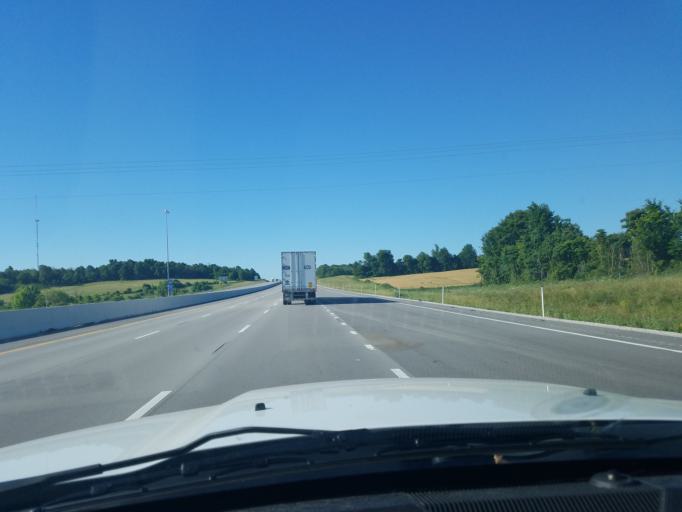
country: US
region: Kentucky
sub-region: Hart County
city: Munfordville
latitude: 37.4544
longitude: -85.8836
